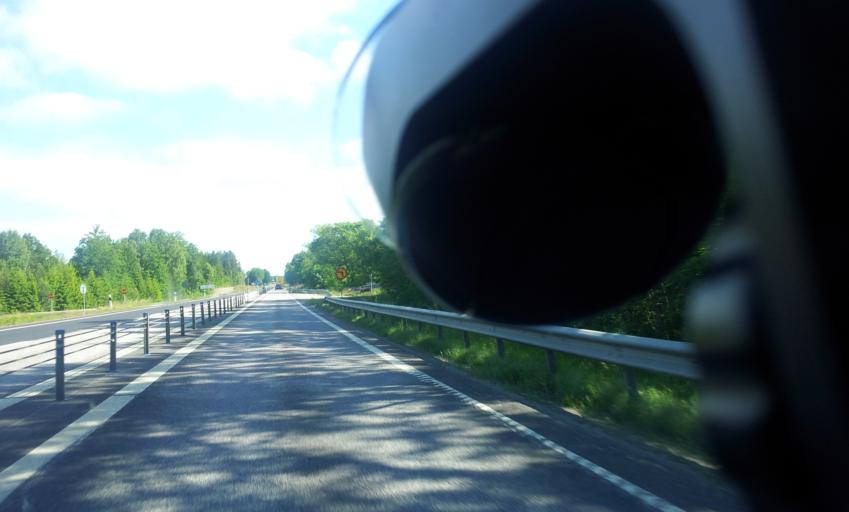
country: SE
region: Kalmar
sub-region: Kalmar Kommun
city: Lindsdal
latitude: 56.8375
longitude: 16.3677
